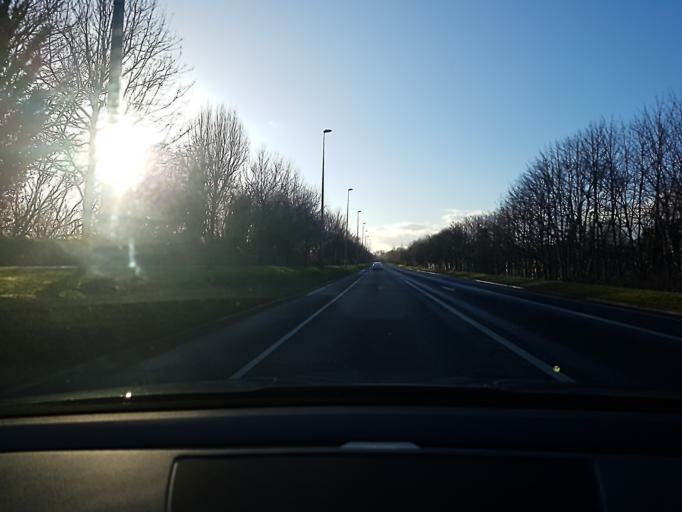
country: IE
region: Munster
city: Moyross
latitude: 52.6611
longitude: -8.6460
